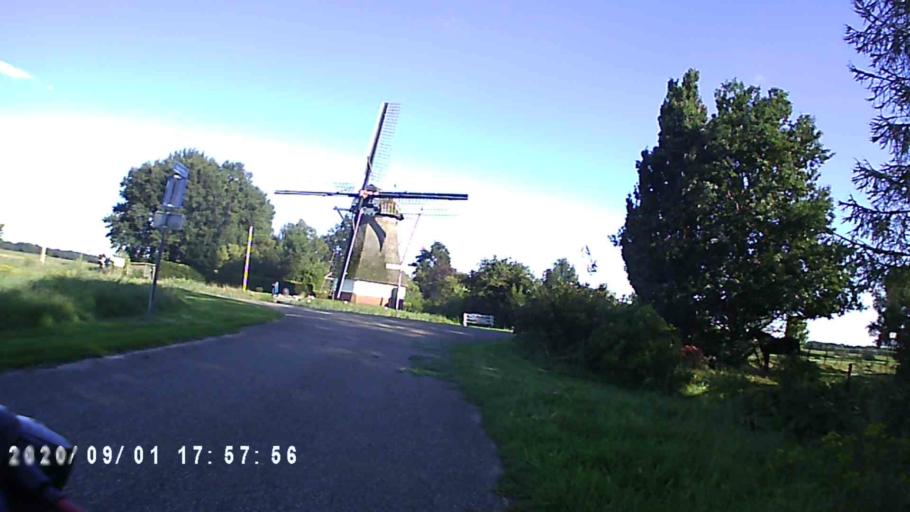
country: NL
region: Groningen
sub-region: Gemeente Slochteren
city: Slochteren
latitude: 53.2063
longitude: 6.7711
